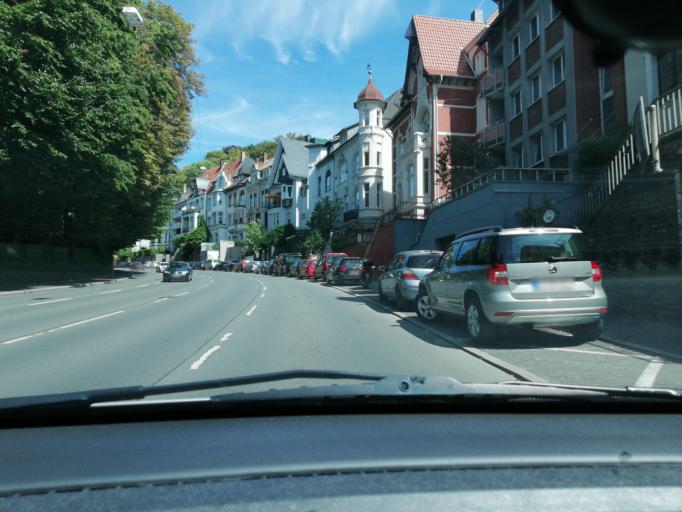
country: DE
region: North Rhine-Westphalia
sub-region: Regierungsbezirk Dusseldorf
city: Wuppertal
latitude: 51.2595
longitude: 7.1321
